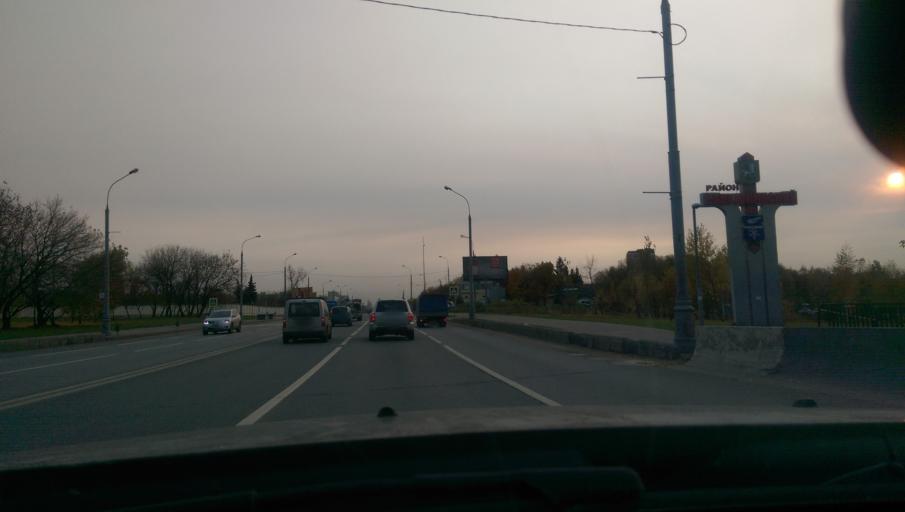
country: RU
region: Moscow
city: Vatutino
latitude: 55.8818
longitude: 37.6708
